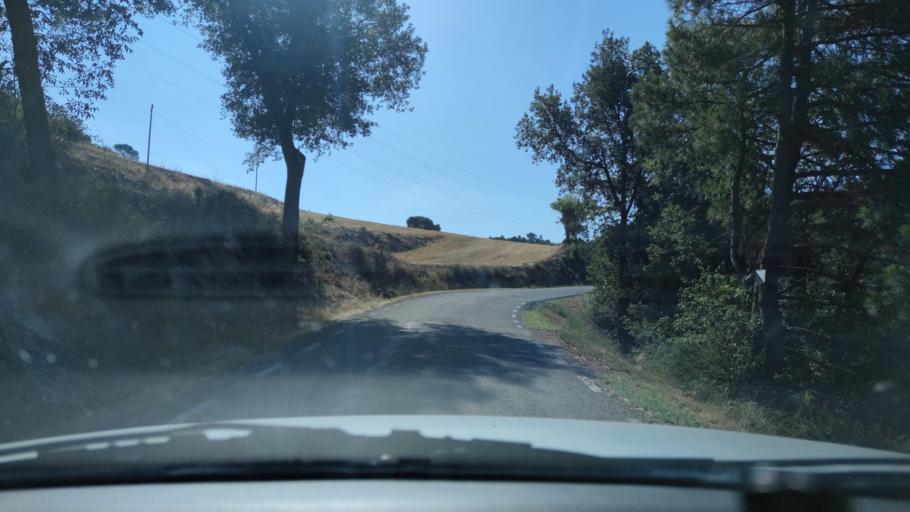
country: ES
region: Catalonia
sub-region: Provincia de Barcelona
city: Pujalt
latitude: 41.7097
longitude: 1.3720
